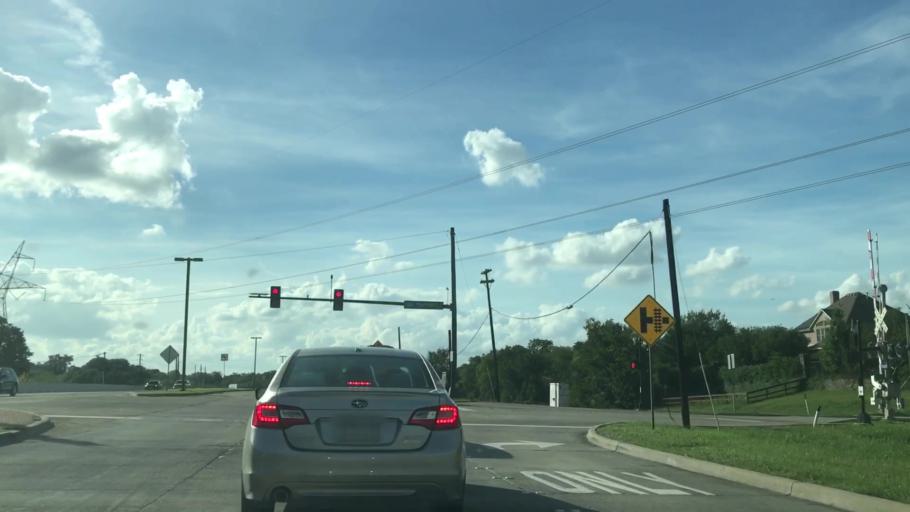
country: US
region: Texas
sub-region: Dallas County
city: Coppell
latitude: 32.9544
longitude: -96.9679
